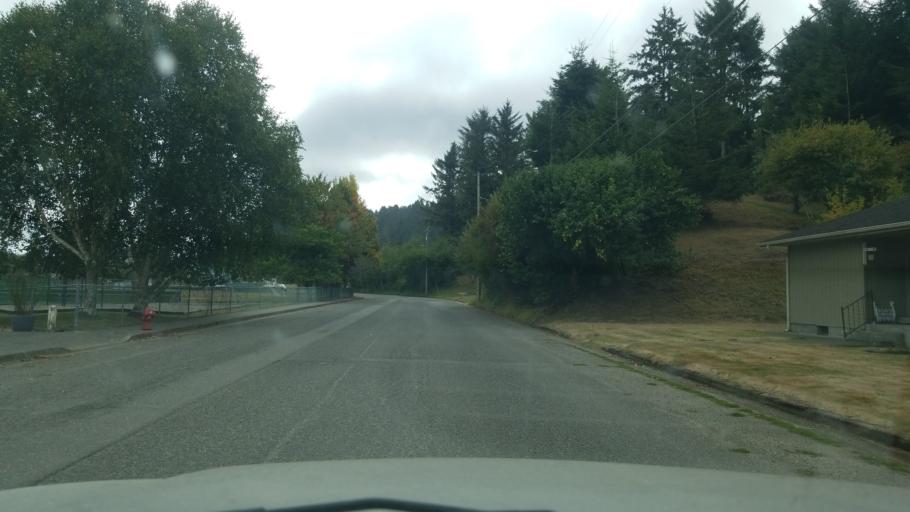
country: US
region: California
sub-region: Humboldt County
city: Ferndale
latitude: 40.5773
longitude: -124.2689
